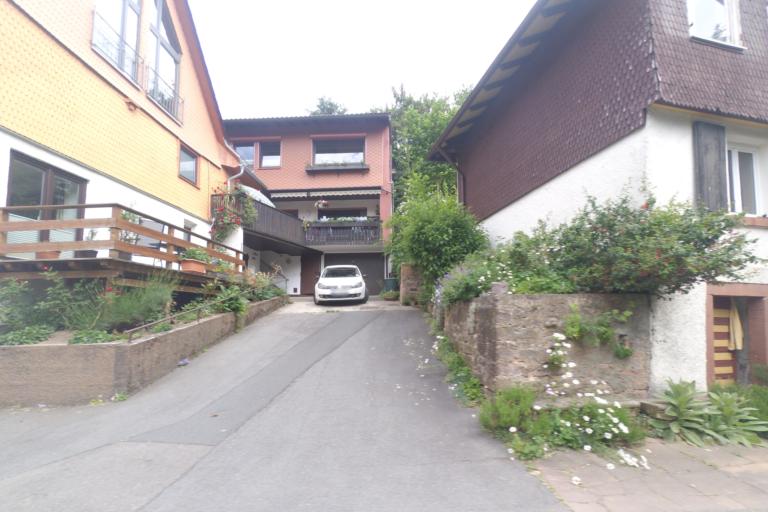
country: DE
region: Hesse
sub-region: Regierungsbezirk Darmstadt
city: Furth
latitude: 49.6353
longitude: 8.8247
